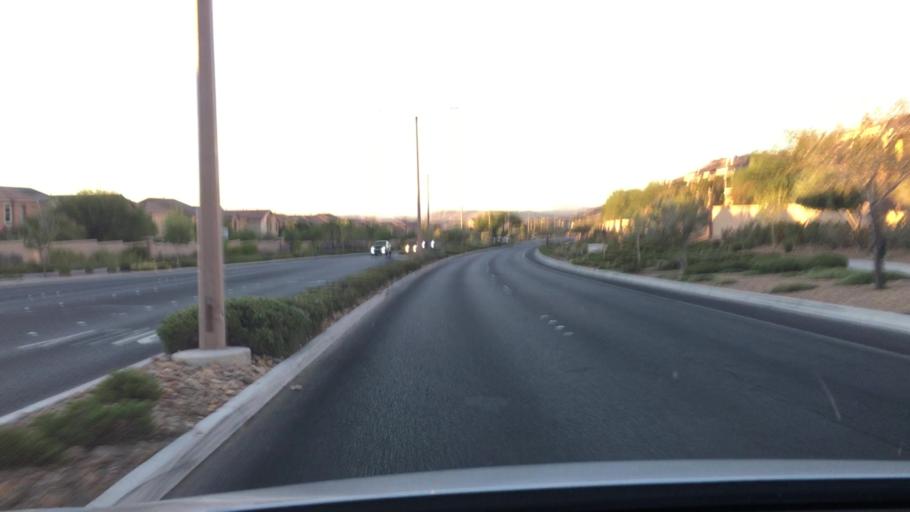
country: US
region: Nevada
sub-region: Clark County
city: Summerlin South
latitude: 36.1638
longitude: -115.3527
